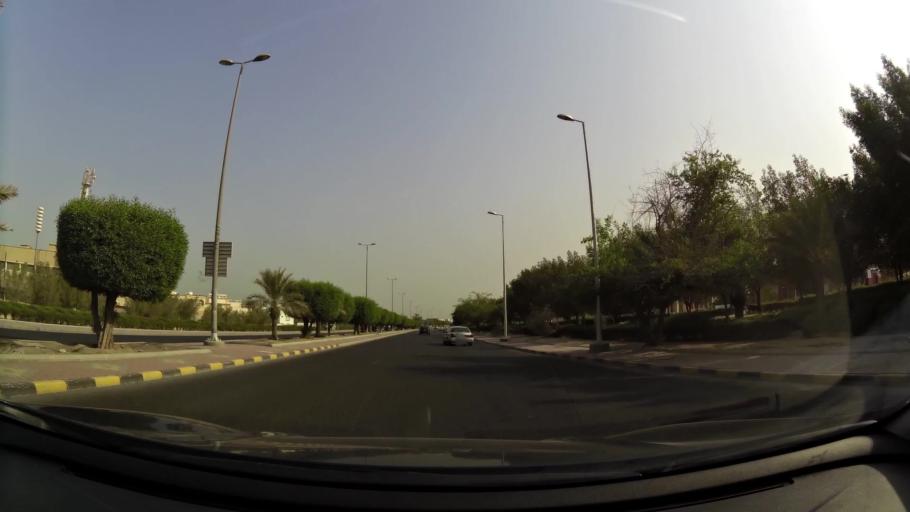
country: KW
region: Mubarak al Kabir
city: Sabah as Salim
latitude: 29.2516
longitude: 48.0651
